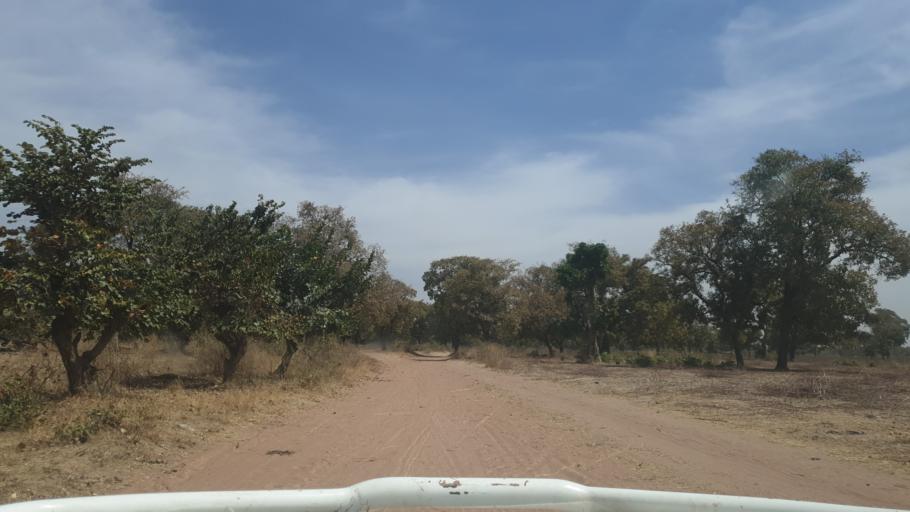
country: ML
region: Sikasso
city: Yorosso
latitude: 12.2957
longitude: -4.6402
